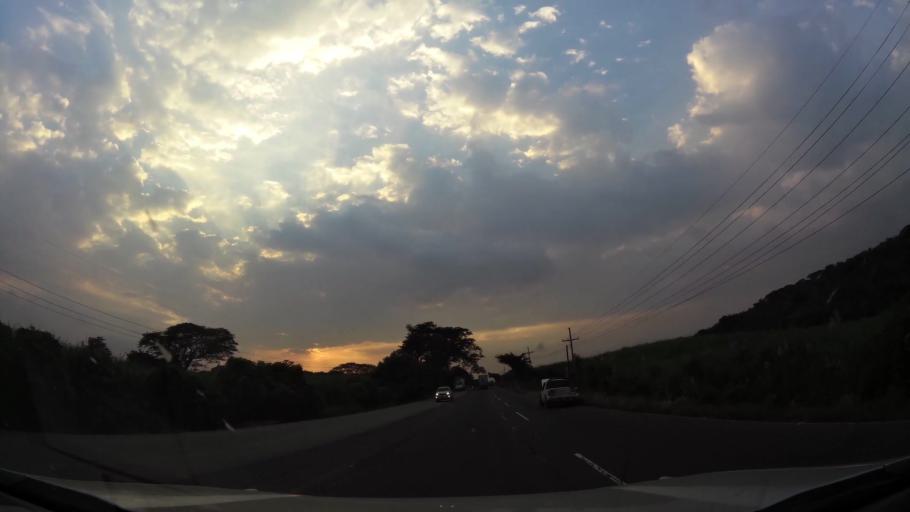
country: GT
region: Escuintla
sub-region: Municipio de Masagua
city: Masagua
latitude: 14.2673
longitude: -90.8822
